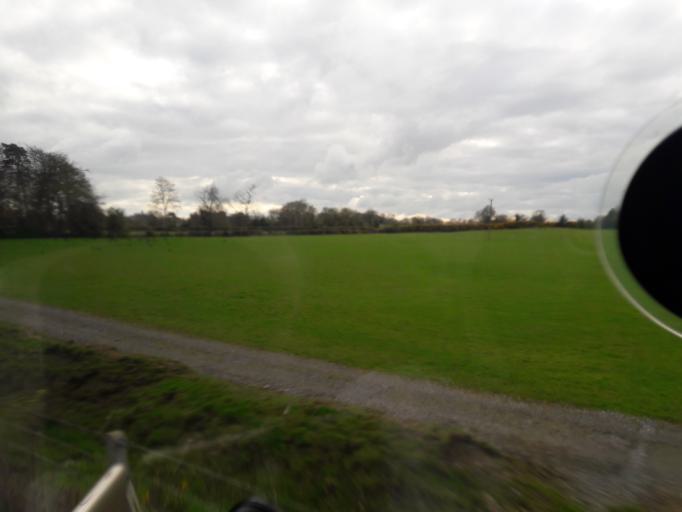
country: IE
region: Leinster
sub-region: An Iarmhi
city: An Muileann gCearr
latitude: 53.6198
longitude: -7.4135
